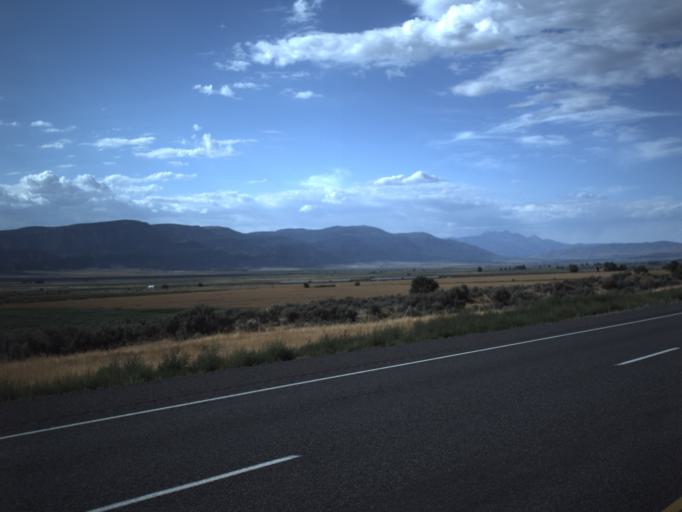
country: US
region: Utah
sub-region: Sanpete County
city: Ephraim
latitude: 39.4146
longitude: -111.5605
